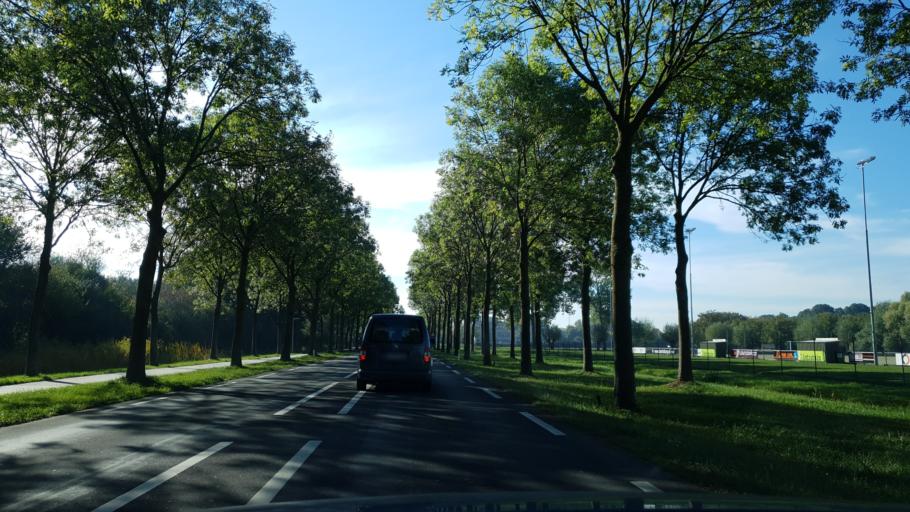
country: NL
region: Gelderland
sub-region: Gemeente Beuningen
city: Beuningen
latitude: 51.8613
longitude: 5.7513
